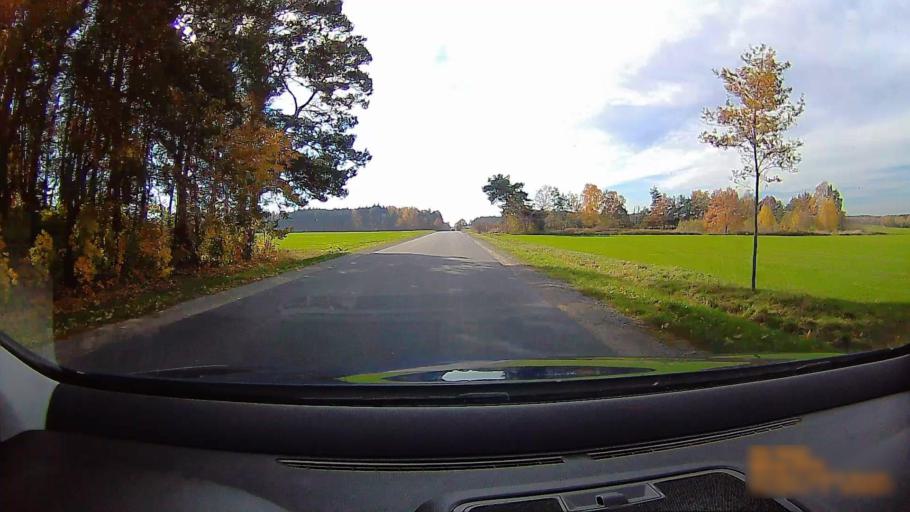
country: PL
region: Greater Poland Voivodeship
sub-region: Powiat ostrzeszowski
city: Doruchow
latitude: 51.3741
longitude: 18.0376
